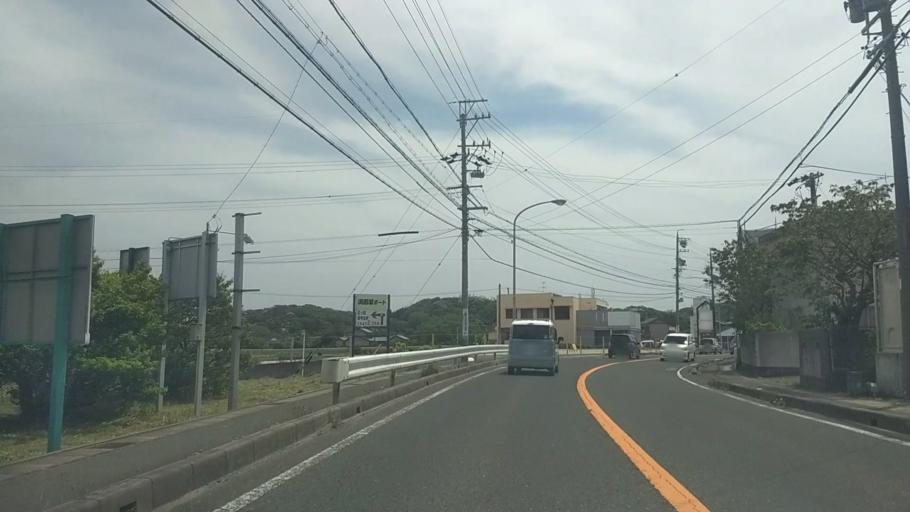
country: JP
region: Shizuoka
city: Kosai-shi
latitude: 34.7041
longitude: 137.5518
